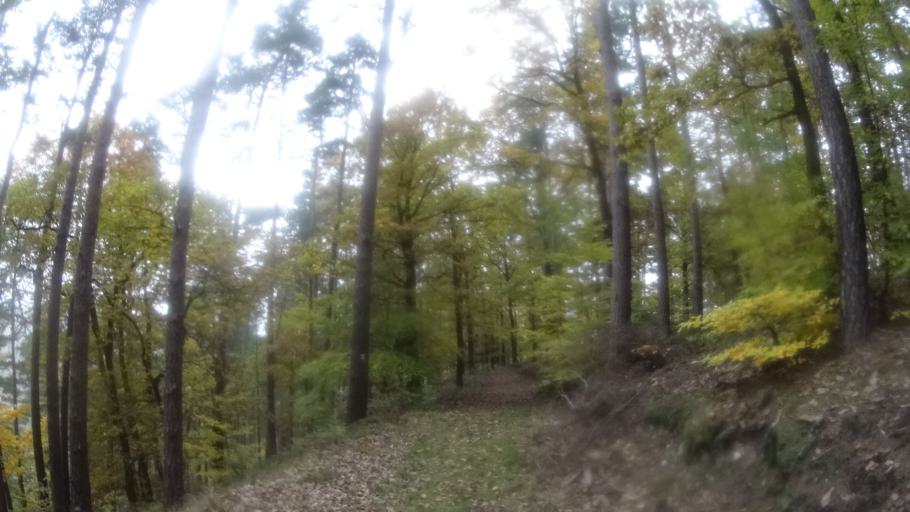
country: DE
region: Thuringia
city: Grosseutersdorf
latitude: 50.7788
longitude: 11.5651
